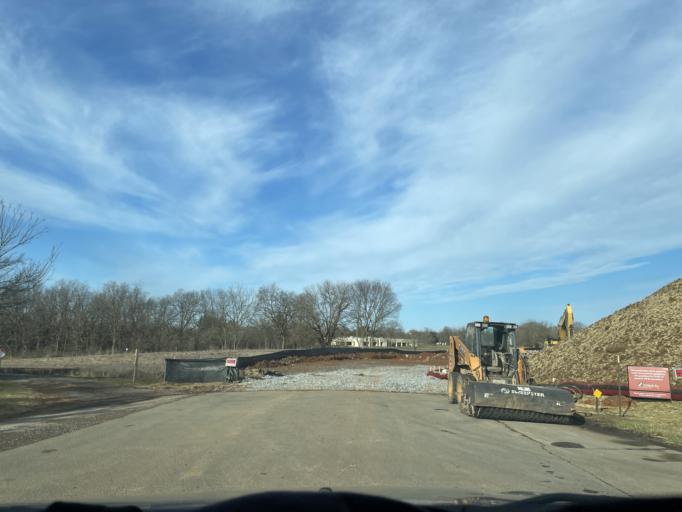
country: US
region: Maryland
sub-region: Washington County
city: Halfway
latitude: 39.6462
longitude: -77.7612
